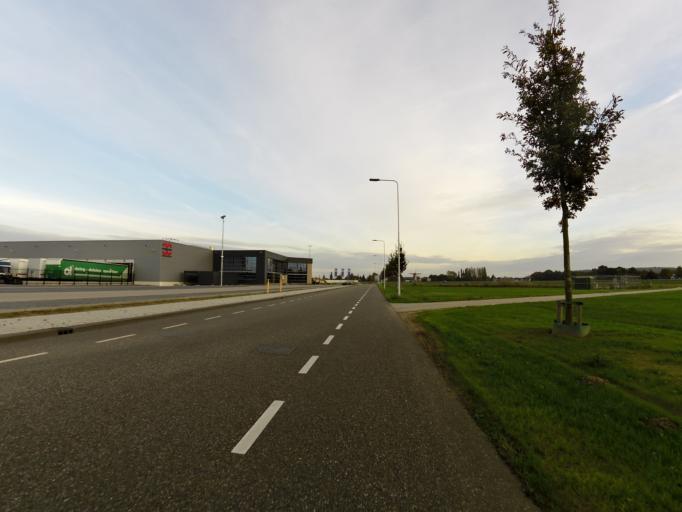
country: NL
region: Gelderland
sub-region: Gemeente Doetinchem
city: Doetinchem
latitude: 51.9467
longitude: 6.2253
